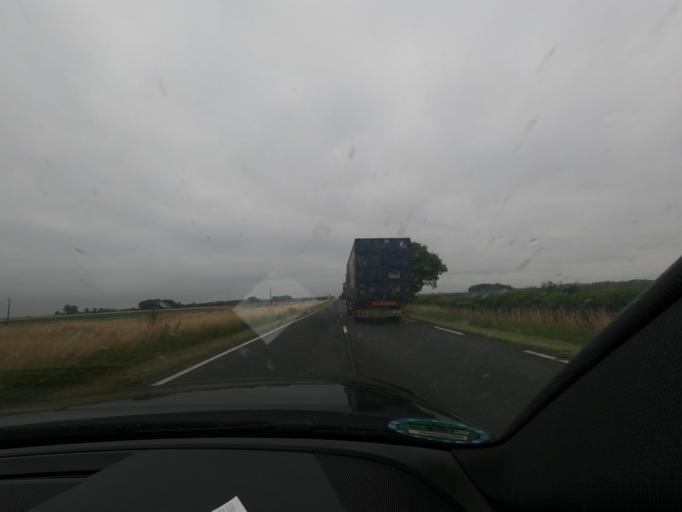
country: FR
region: Picardie
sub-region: Departement de la Somme
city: Harbonnieres
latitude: 49.7788
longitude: 2.5976
